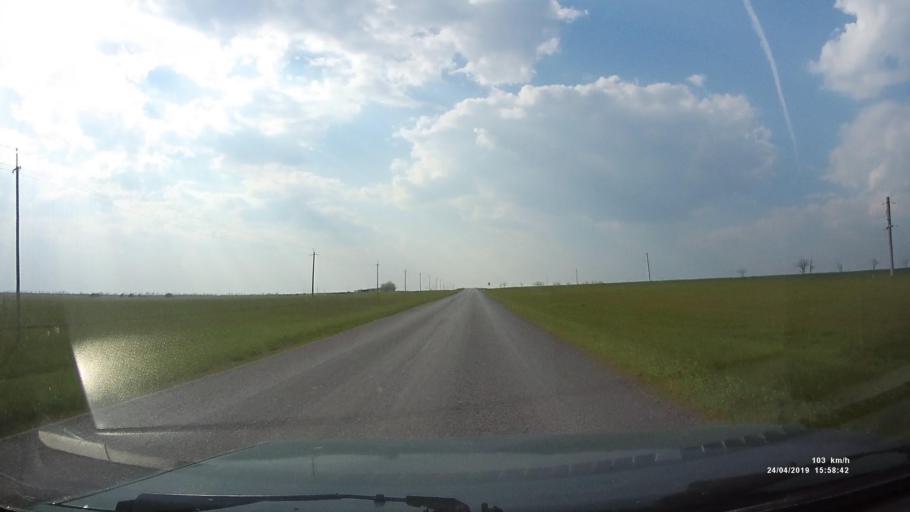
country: RU
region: Kalmykiya
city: Yashalta
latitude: 46.6167
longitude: 42.4853
